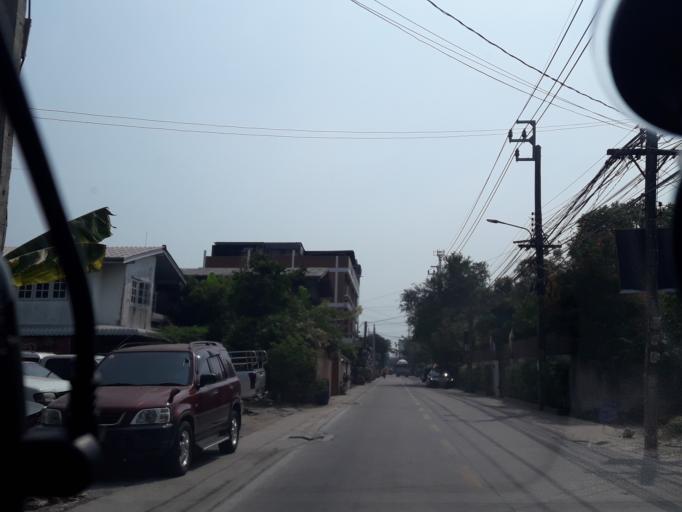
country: TH
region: Bangkok
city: Min Buri
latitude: 13.8155
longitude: 100.7053
